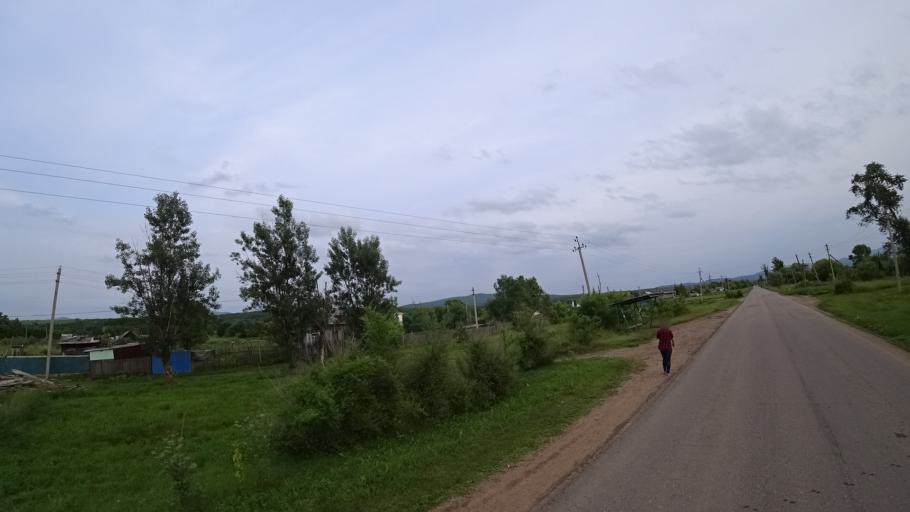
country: RU
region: Primorskiy
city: Novosysoyevka
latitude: 44.2380
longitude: 133.3692
